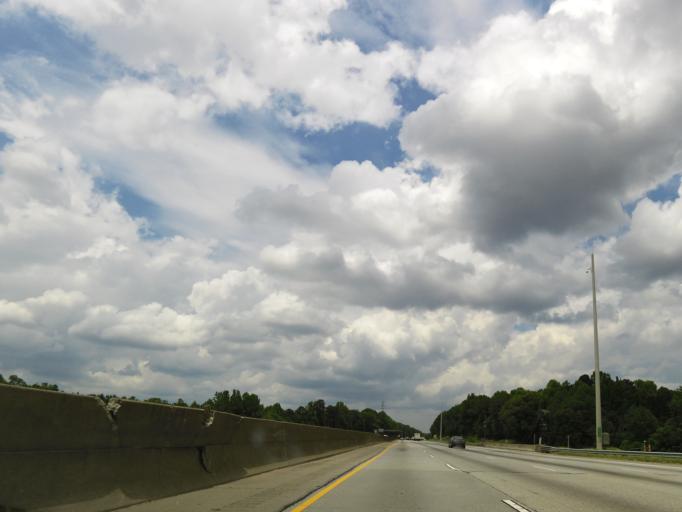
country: US
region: Georgia
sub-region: Fulton County
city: East Point
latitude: 33.7221
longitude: -84.5027
